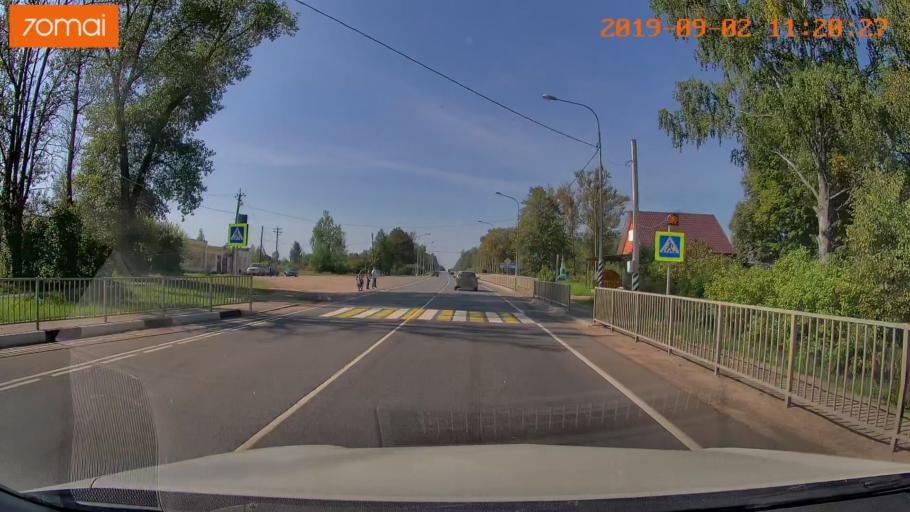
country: RU
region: Smolensk
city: Roslavl'
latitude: 54.0416
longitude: 33.0523
